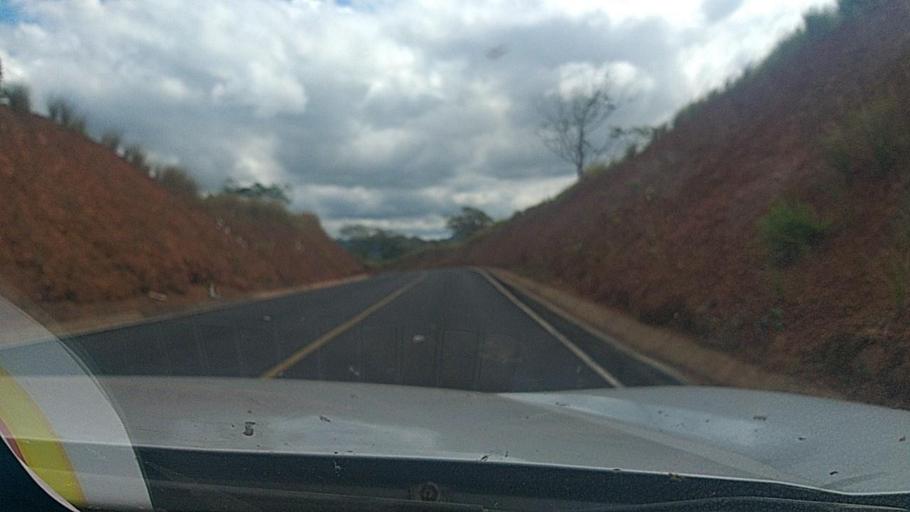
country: NI
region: Atlantico Sur
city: Muelle de los Bueyes
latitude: 12.1293
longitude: -84.4349
